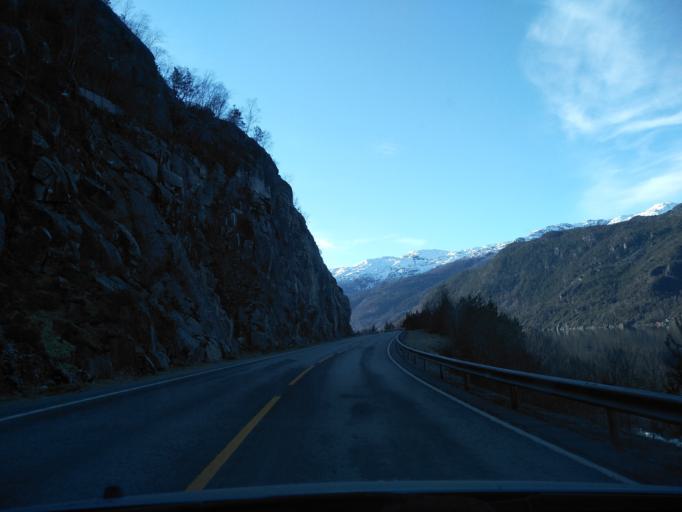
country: NO
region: Rogaland
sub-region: Sauda
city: Sauda
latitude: 59.8356
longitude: 6.2934
